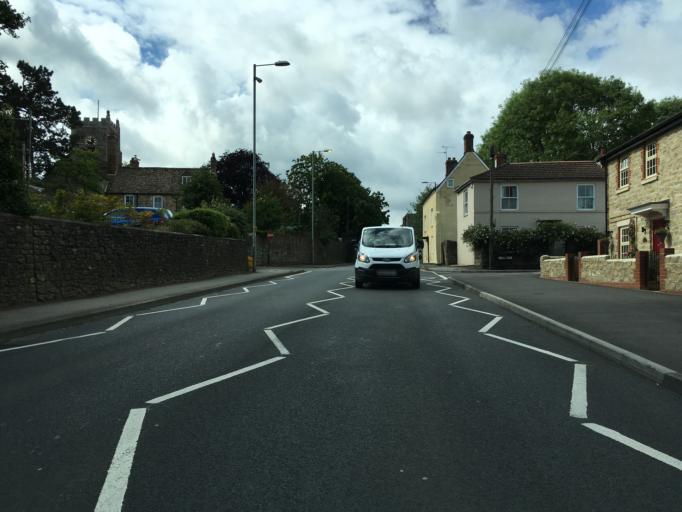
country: GB
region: England
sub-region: Borough of Swindon
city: Highworth
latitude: 51.6321
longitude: -1.7113
